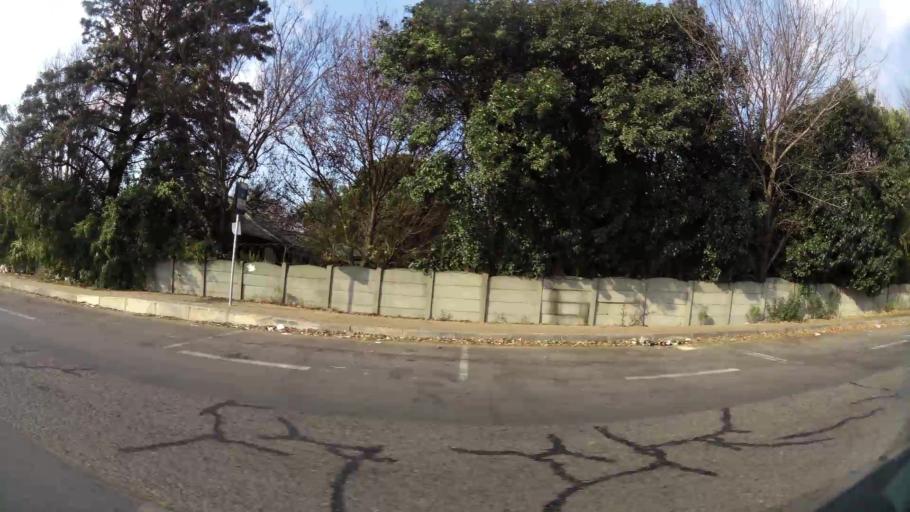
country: ZA
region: Gauteng
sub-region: City of Johannesburg Metropolitan Municipality
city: Modderfontein
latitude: -26.1011
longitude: 28.1957
